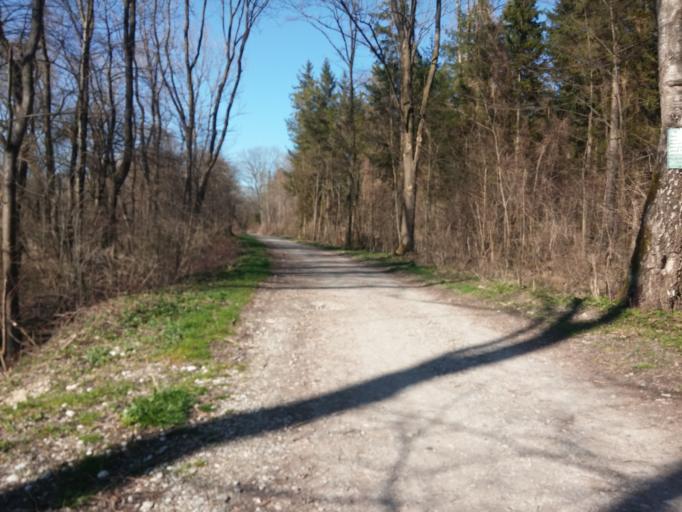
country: DE
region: Bavaria
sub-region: Upper Bavaria
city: Ismaning
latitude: 48.2389
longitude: 11.6739
